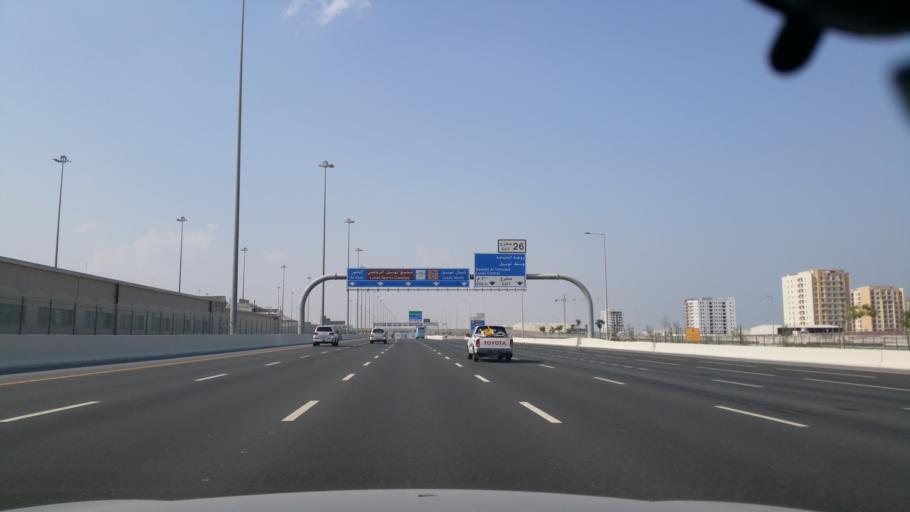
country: QA
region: Baladiyat Umm Salal
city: Umm Salal Muhammad
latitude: 25.4205
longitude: 51.4869
